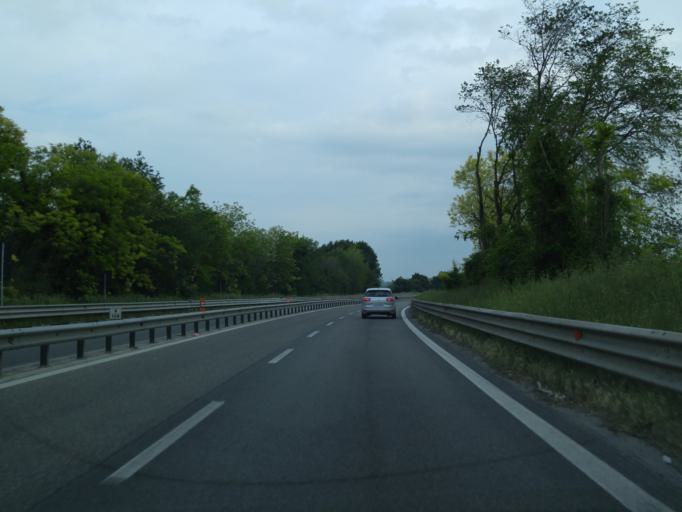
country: IT
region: The Marches
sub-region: Provincia di Pesaro e Urbino
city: Bellocchi
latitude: 43.8101
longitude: 13.0184
